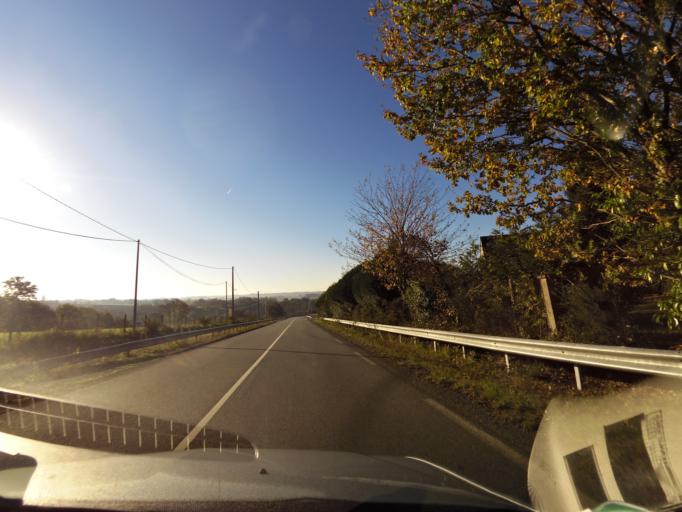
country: FR
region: Brittany
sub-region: Departement d'Ille-et-Vilaine
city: Crevin
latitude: 47.9271
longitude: -1.6739
